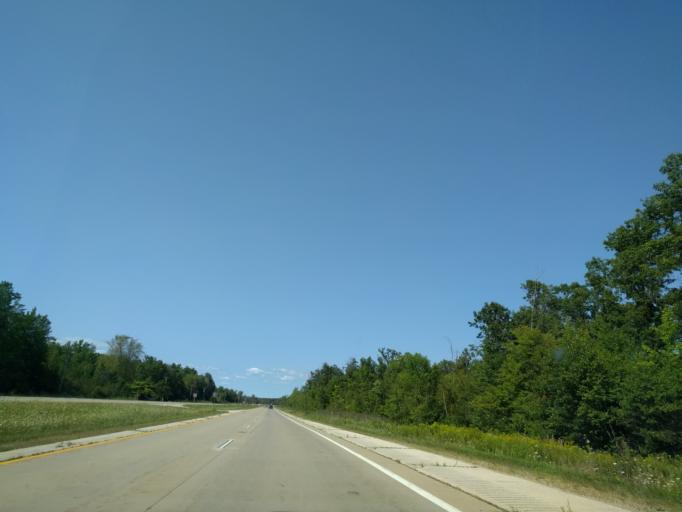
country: US
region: Wisconsin
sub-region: Oconto County
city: Oconto
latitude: 44.8550
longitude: -87.8990
